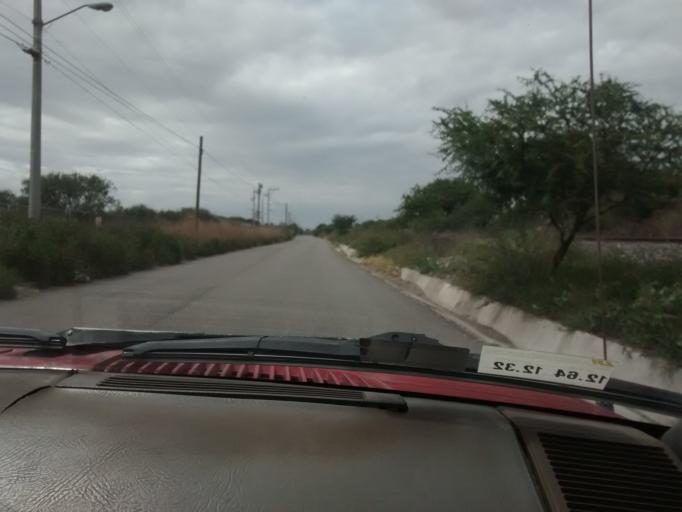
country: MX
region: Puebla
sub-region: Santiago Miahuatlan
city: San Jose Monte Chiquito
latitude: 18.4960
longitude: -97.4220
